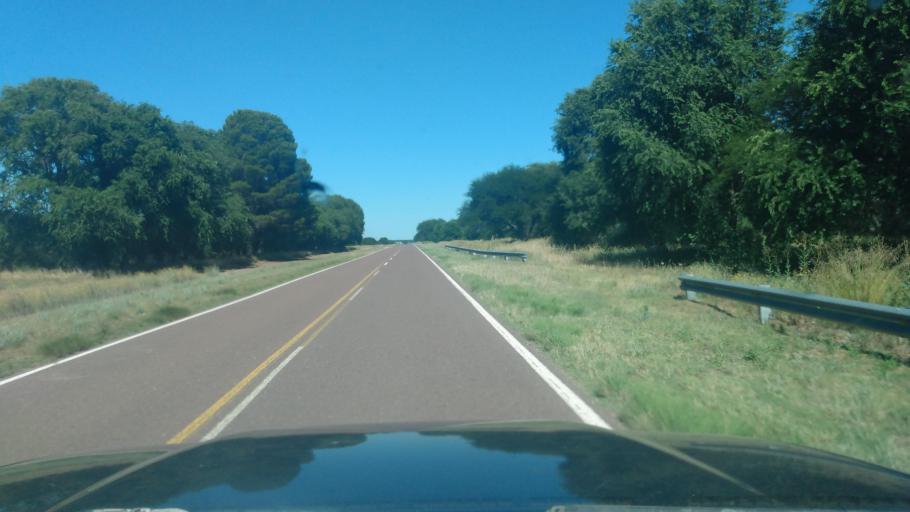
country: AR
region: La Pampa
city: General Acha
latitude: -37.4178
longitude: -64.8565
